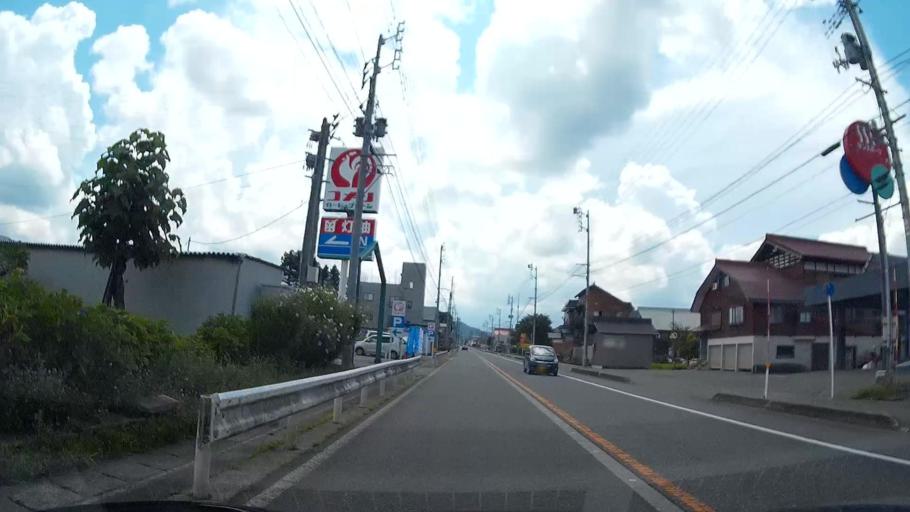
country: JP
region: Niigata
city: Tokamachi
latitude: 37.0225
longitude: 138.6591
